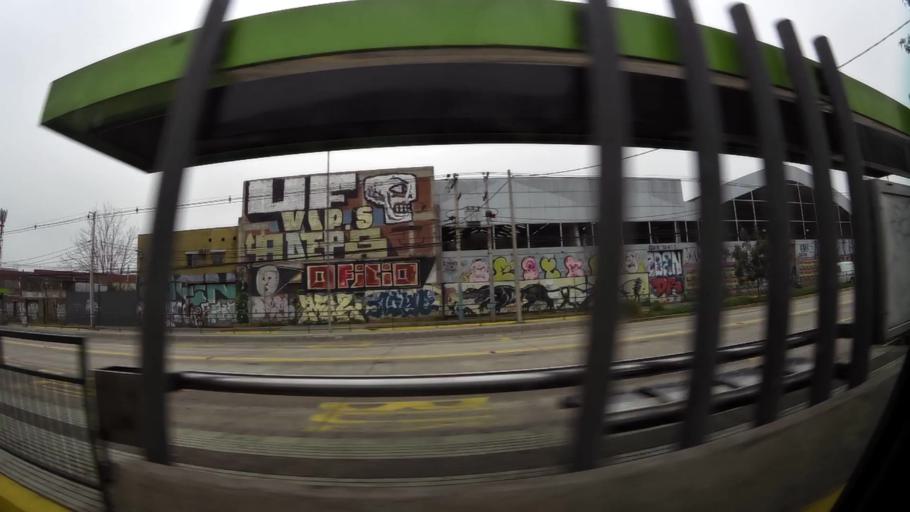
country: CL
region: Santiago Metropolitan
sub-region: Provincia de Santiago
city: Santiago
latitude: -33.4888
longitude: -70.6408
